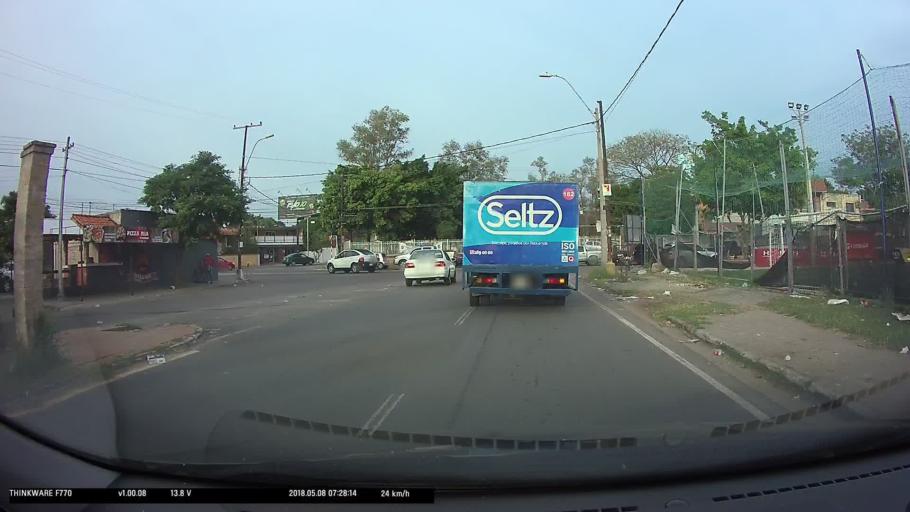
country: PY
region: Central
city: Fernando de la Mora
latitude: -25.2761
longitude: -57.5518
